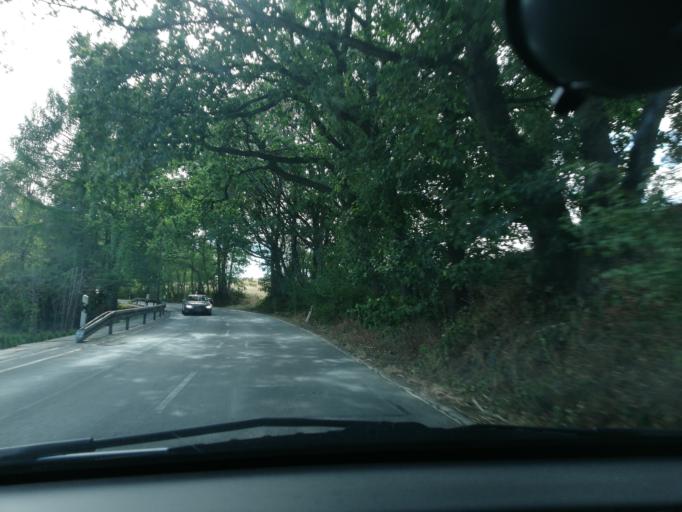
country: DE
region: North Rhine-Westphalia
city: Sprockhovel
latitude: 51.3047
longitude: 7.2213
